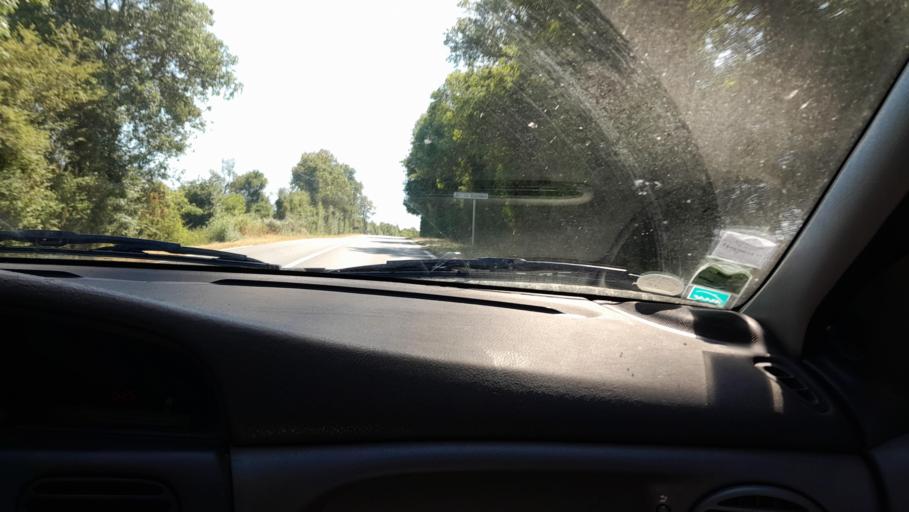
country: FR
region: Pays de la Loire
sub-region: Departement de la Loire-Atlantique
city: Saint-Gereon
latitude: 47.3637
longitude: -1.2289
